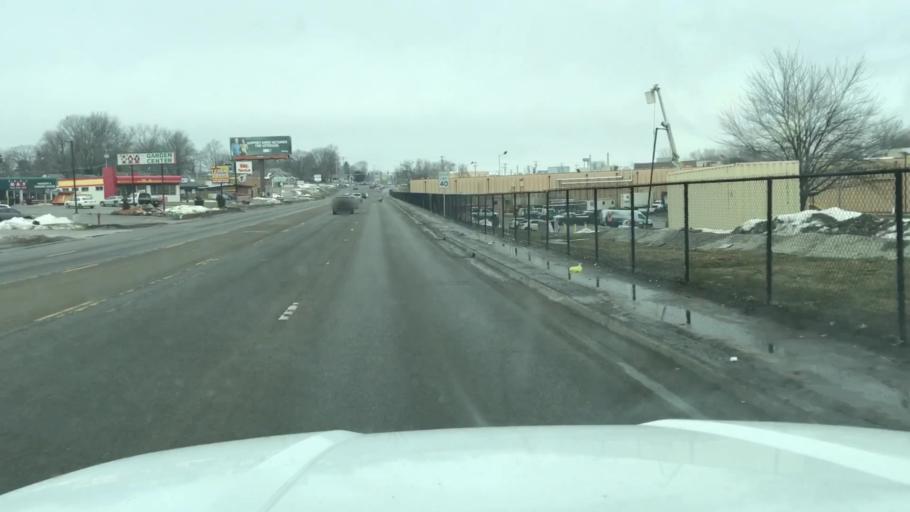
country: US
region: Missouri
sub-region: Buchanan County
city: Saint Joseph
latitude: 39.7891
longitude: -94.8073
